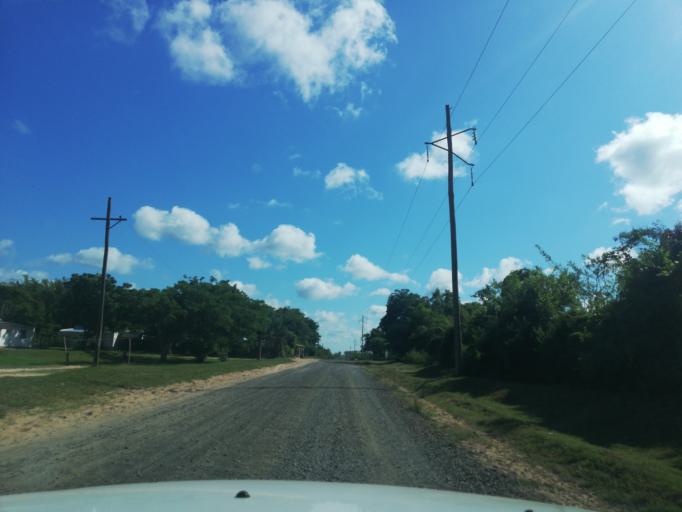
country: AR
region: Corrientes
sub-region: Departamento de San Miguel
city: San Miguel
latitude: -27.9875
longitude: -57.5855
